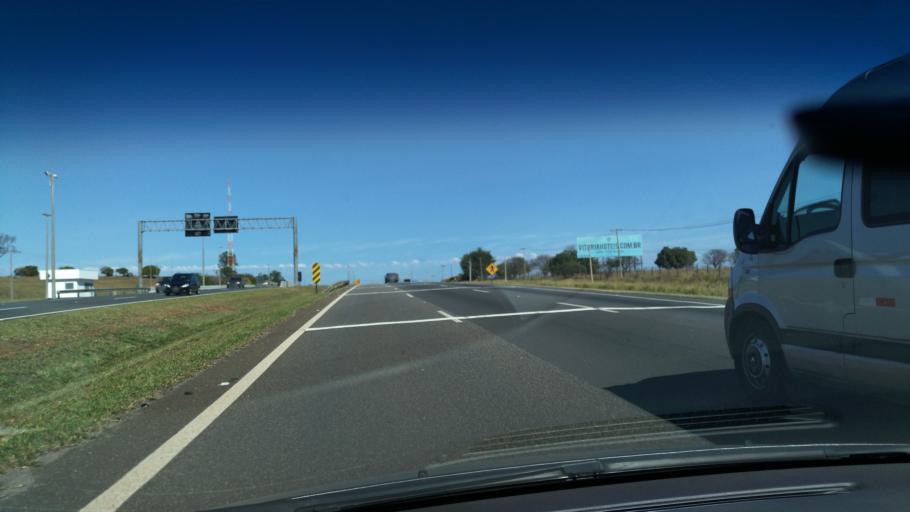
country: BR
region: Sao Paulo
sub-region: Jaguariuna
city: Jaguariuna
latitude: -22.7950
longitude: -47.0323
